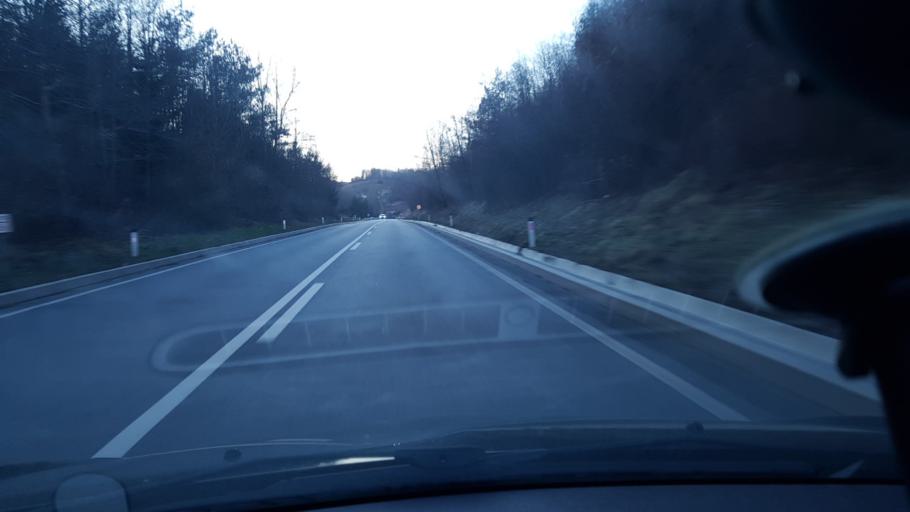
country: SI
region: Rogaska Slatina
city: Rogaska Slatina
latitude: 46.2420
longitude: 15.6632
